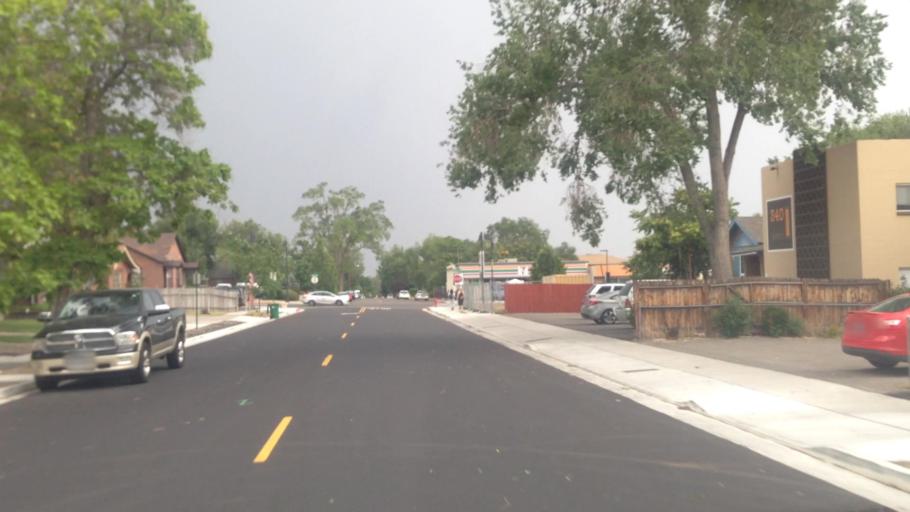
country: US
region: Nevada
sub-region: Washoe County
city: Reno
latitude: 39.5183
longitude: -119.8044
